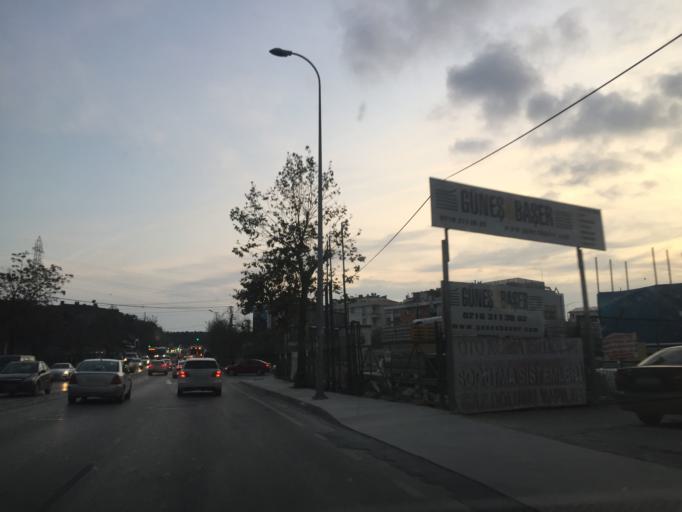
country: TR
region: Istanbul
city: Samandira
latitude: 40.9773
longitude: 29.2199
